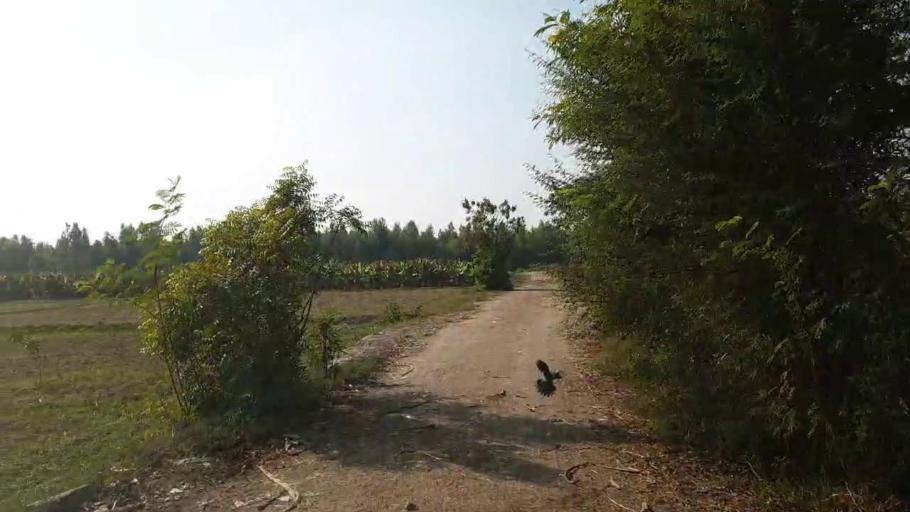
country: PK
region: Sindh
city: Tando Adam
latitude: 25.6617
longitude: 68.5696
